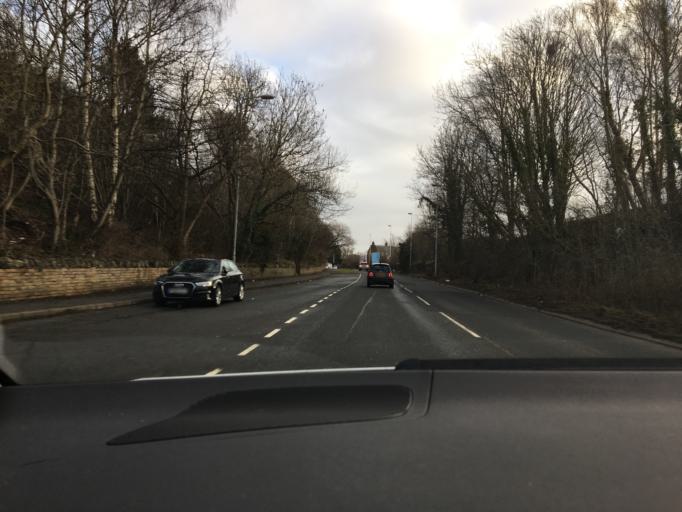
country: GB
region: Scotland
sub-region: Midlothian
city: Dalkeith
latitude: 55.8711
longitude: -3.0734
